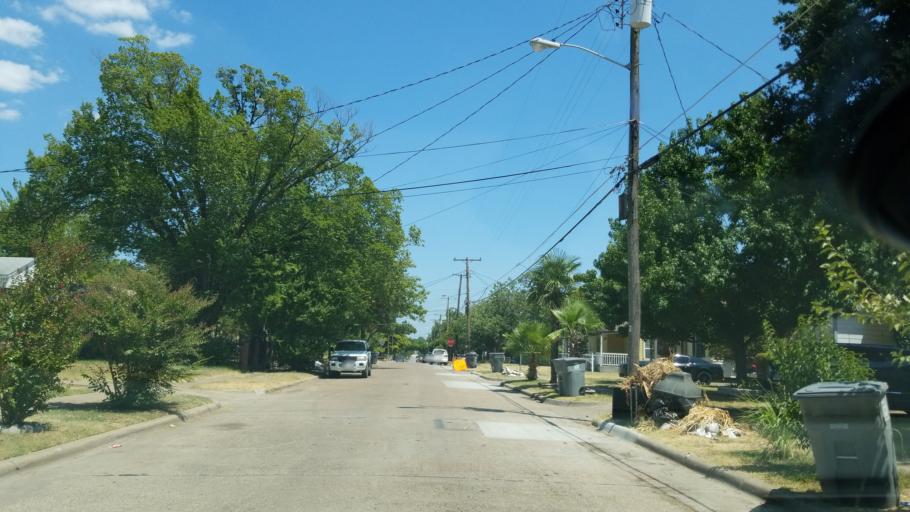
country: US
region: Texas
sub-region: Dallas County
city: Cockrell Hill
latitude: 32.7284
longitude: -96.8862
